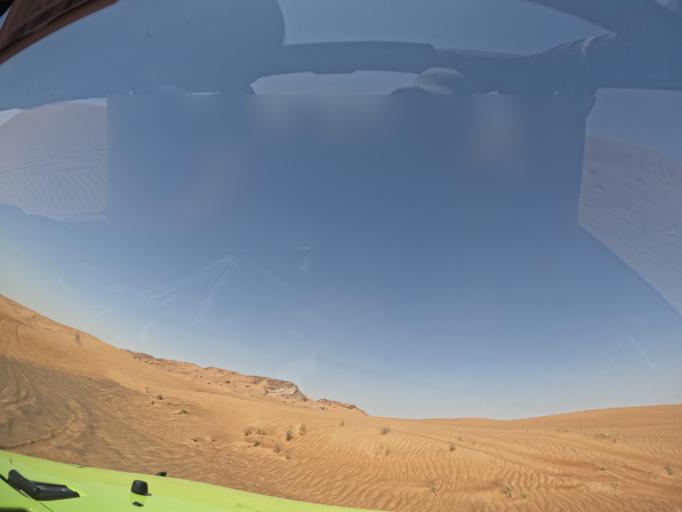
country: AE
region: Ash Shariqah
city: Adh Dhayd
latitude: 25.0198
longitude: 55.7408
